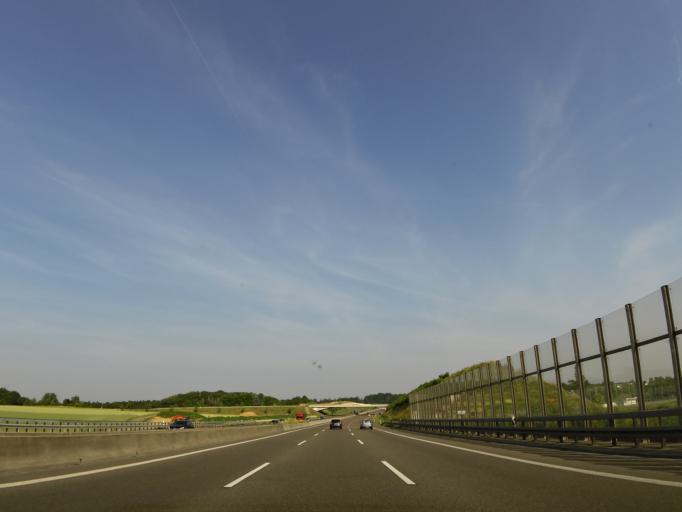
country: DE
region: Baden-Wuerttemberg
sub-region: Regierungsbezirk Stuttgart
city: Rutesheim
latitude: 48.7999
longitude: 8.9449
